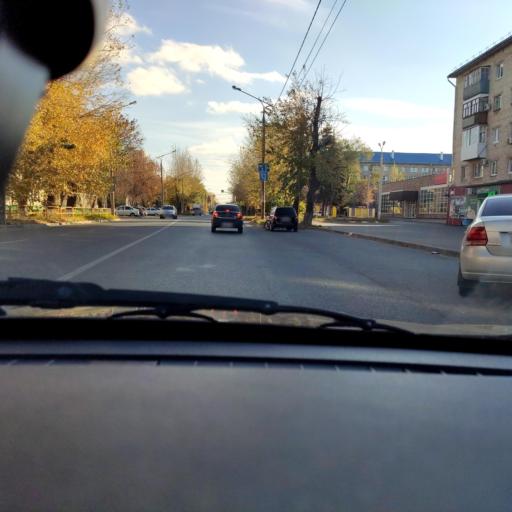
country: RU
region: Samara
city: Tol'yatti
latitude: 53.5323
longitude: 49.4115
